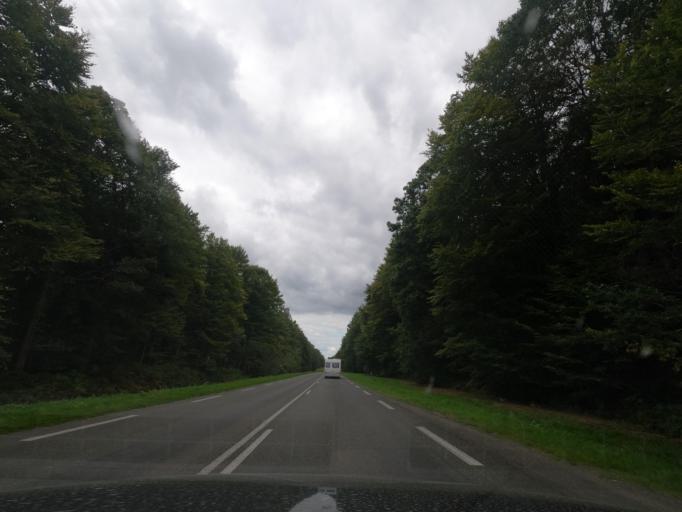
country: FR
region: Brittany
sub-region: Departement d'Ille-et-Vilaine
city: Landean
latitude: 48.3977
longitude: -1.1613
